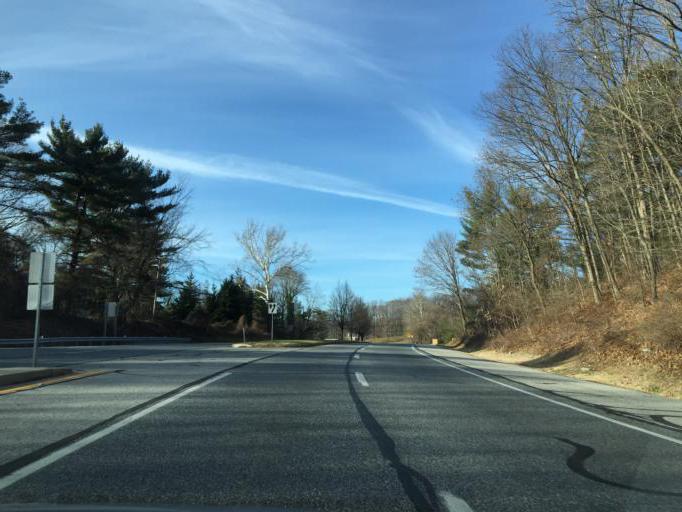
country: US
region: Maryland
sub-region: Baltimore County
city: Lutherville
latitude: 39.4008
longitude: -76.6283
